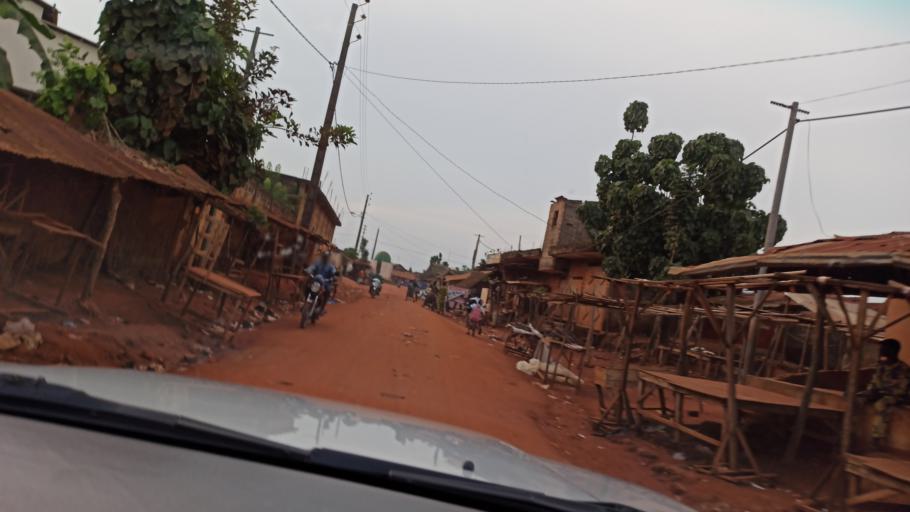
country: BJ
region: Queme
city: Porto-Novo
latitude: 6.5310
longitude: 2.6639
